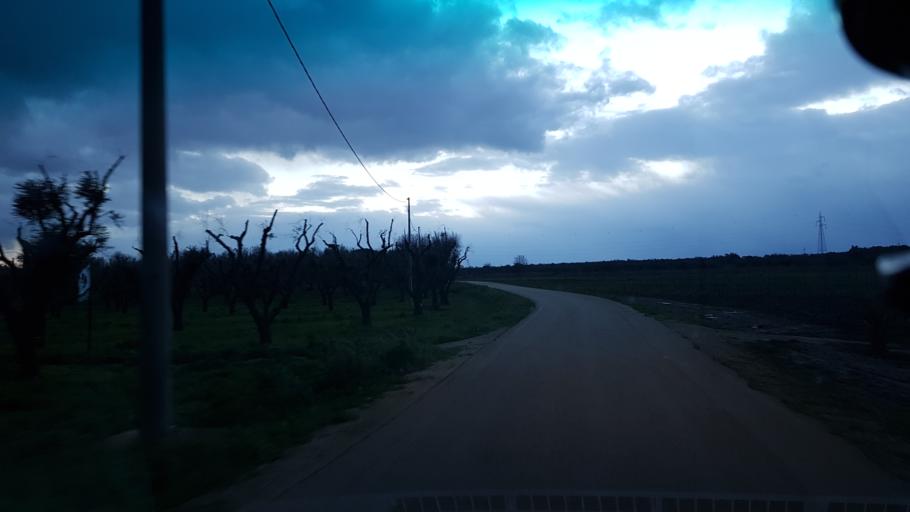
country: IT
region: Apulia
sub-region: Provincia di Brindisi
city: Torchiarolo
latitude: 40.5142
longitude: 18.0283
